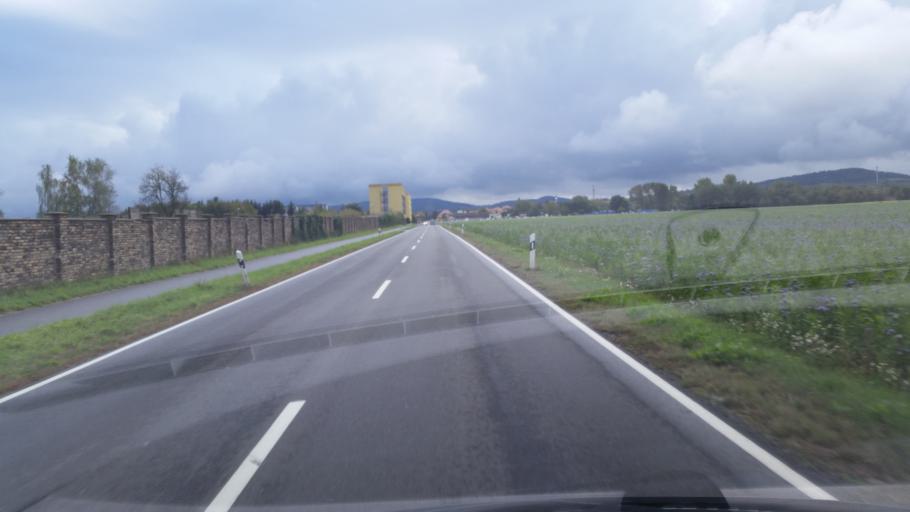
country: DE
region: Saxony
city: Kamenz
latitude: 51.2962
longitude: 14.1156
